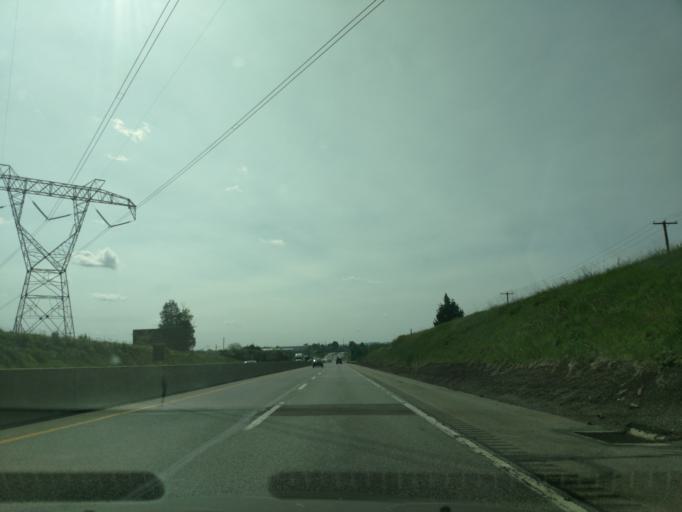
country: US
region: Pennsylvania
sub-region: Lancaster County
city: Swartzville
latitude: 40.2144
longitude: -76.0644
